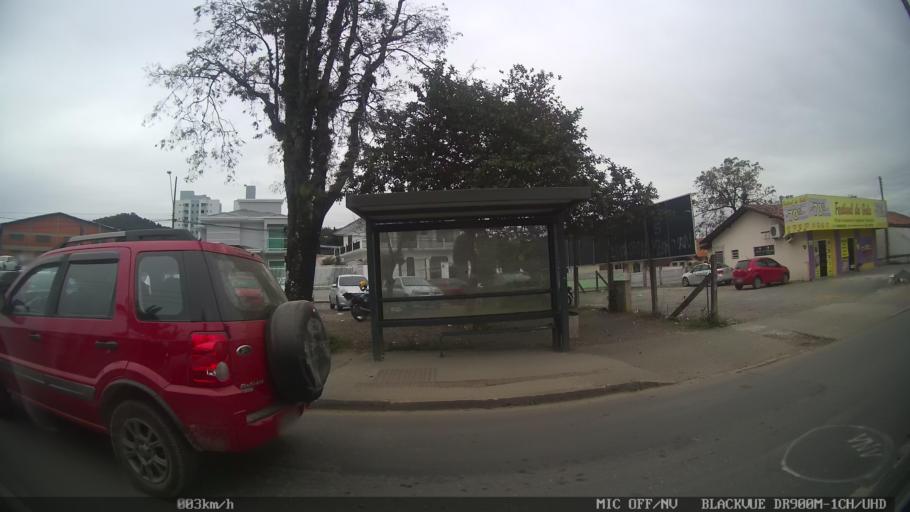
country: BR
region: Santa Catarina
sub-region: Joinville
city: Joinville
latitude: -26.2713
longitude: -48.8217
